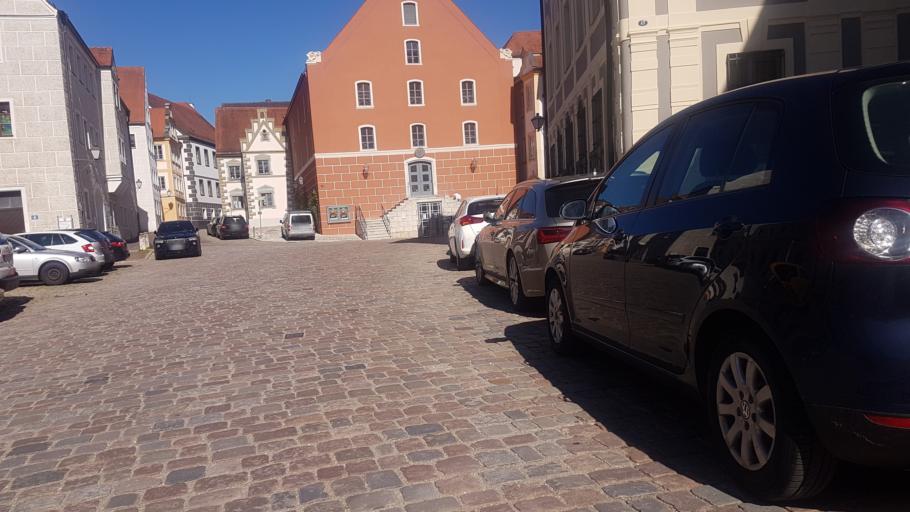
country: DE
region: Bavaria
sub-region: Upper Bavaria
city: Neuburg an der Donau
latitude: 48.7362
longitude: 11.1803
